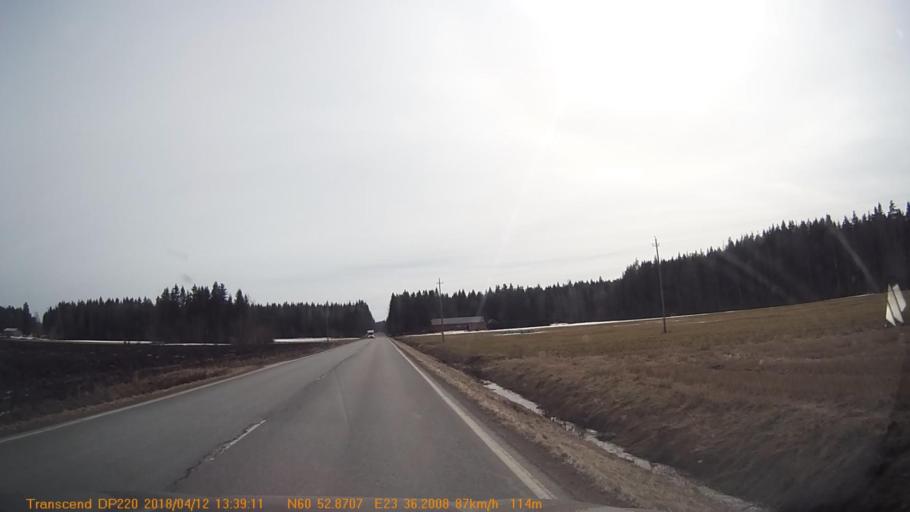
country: FI
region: Haeme
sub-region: Forssa
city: Forssa
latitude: 60.8808
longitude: 23.6035
